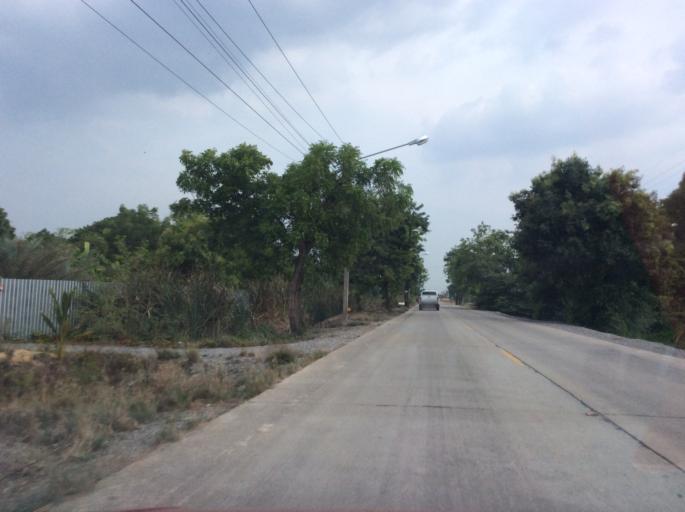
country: TH
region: Pathum Thani
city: Lam Luk Ka
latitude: 13.9722
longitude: 100.7263
